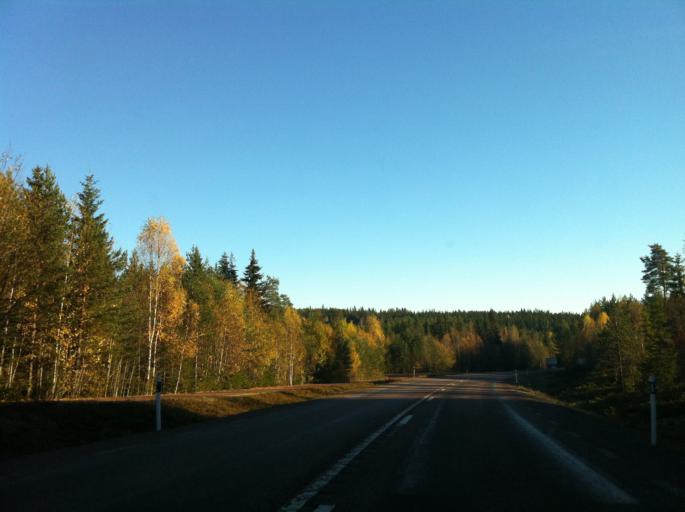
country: SE
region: Dalarna
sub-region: Faluns Kommun
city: Bjursas
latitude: 60.7827
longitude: 15.3106
